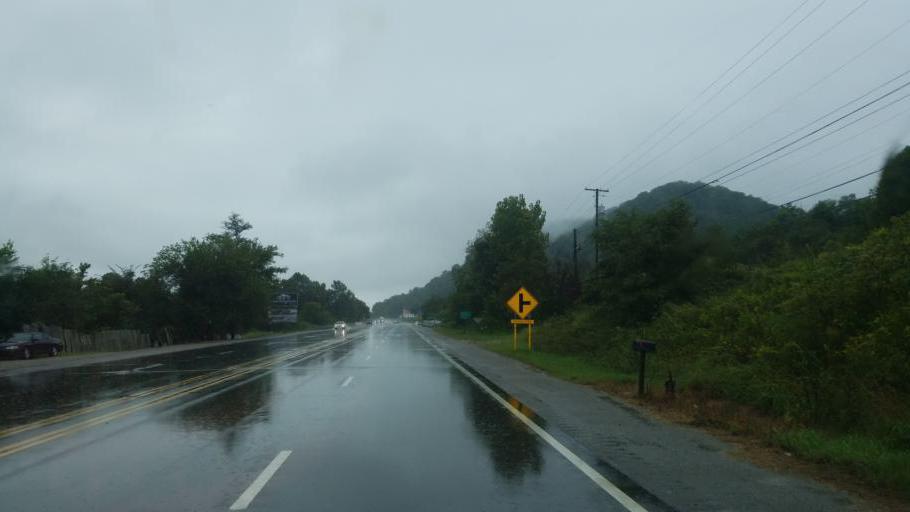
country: US
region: Ohio
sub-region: Scioto County
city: West Portsmouth
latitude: 38.7255
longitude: -83.0429
